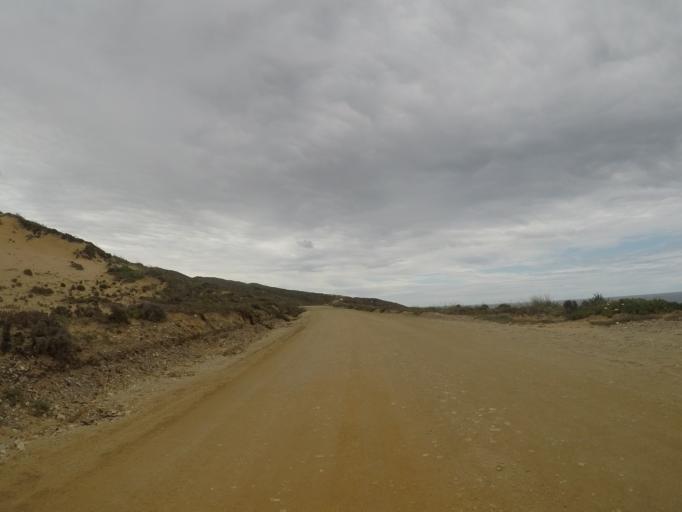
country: PT
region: Beja
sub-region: Odemira
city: Vila Nova de Milfontes
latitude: 37.6432
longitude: -8.8063
